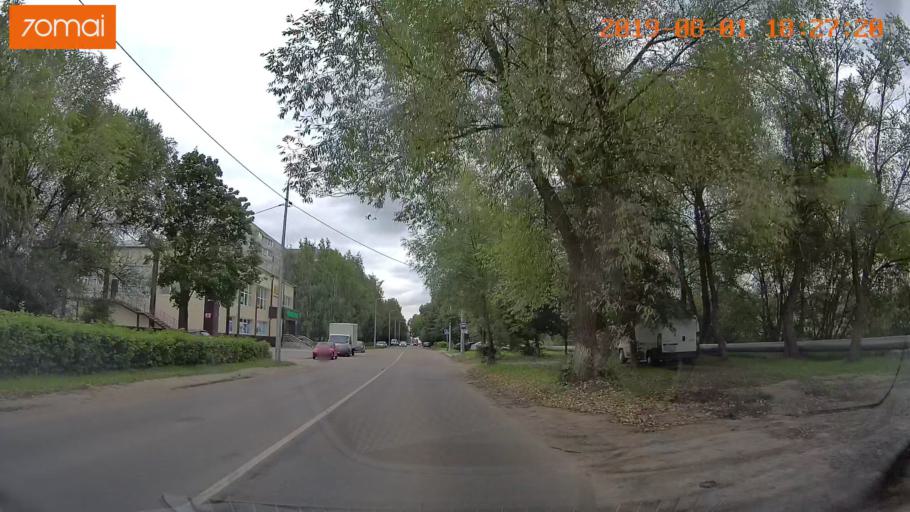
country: RU
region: Moskovskaya
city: Voskresensk
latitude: 55.3129
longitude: 38.6429
